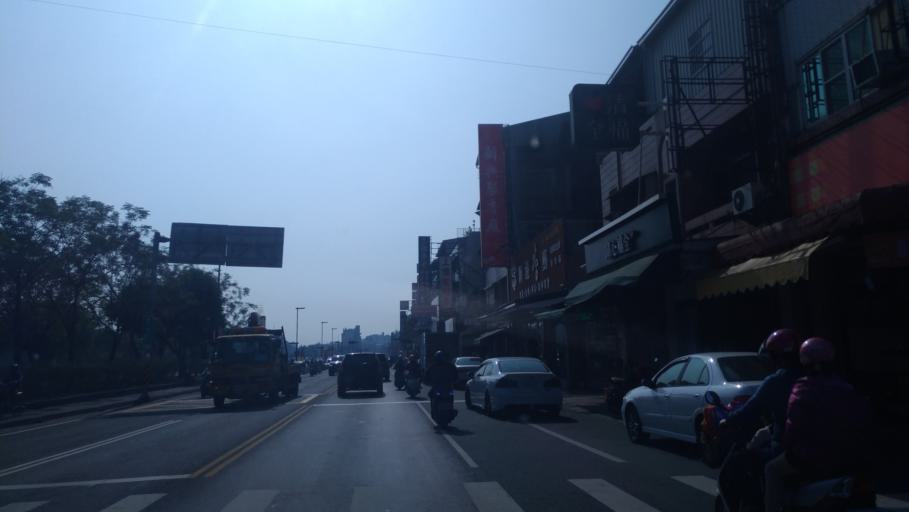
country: TW
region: Taiwan
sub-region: Chiayi
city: Jiayi Shi
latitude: 23.4948
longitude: 120.4439
